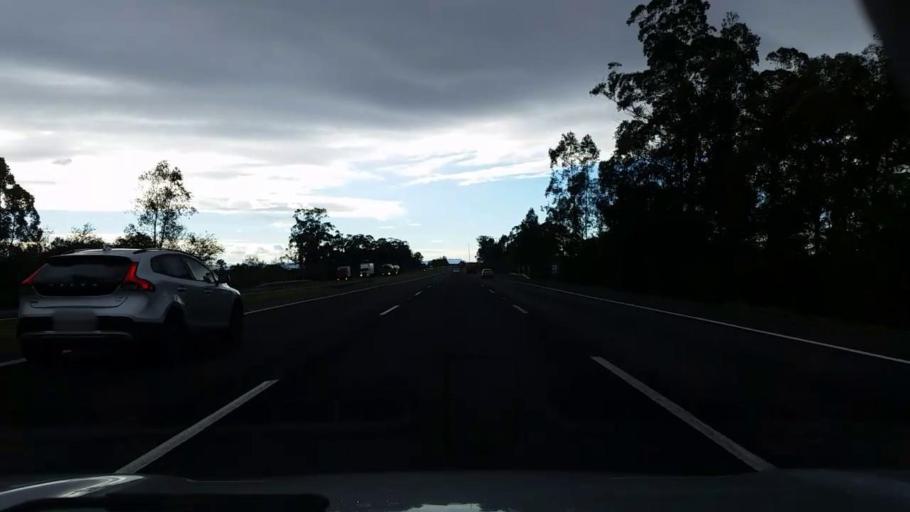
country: BR
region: Rio Grande do Sul
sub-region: Taquara
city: Taquara
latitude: -29.8899
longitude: -50.6932
